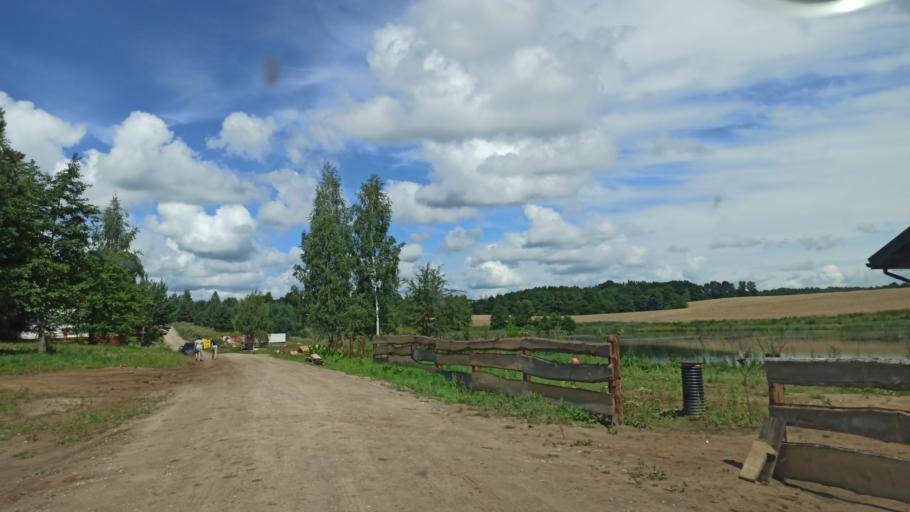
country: PL
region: Warmian-Masurian Voivodeship
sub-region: Powiat ostrodzki
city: Morag
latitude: 53.8535
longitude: 20.0666
